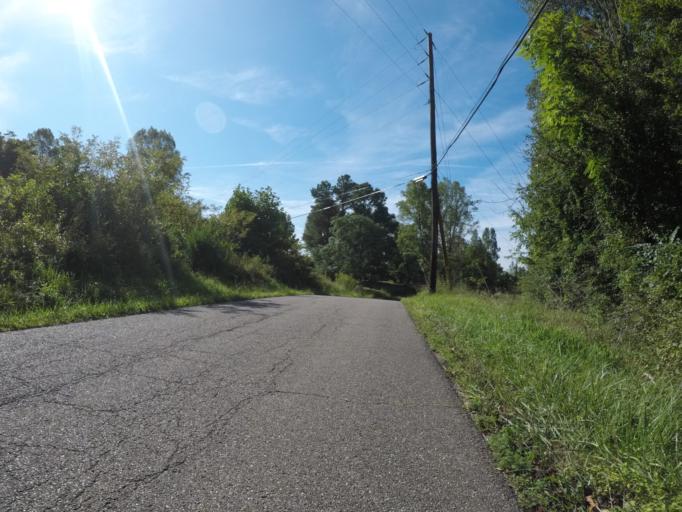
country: US
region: West Virginia
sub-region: Cabell County
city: Huntington
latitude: 38.4642
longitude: -82.4630
